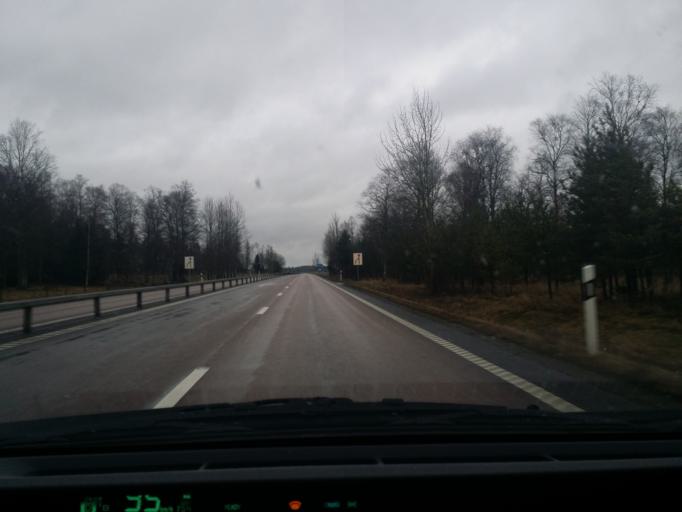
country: SE
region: Vaestmanland
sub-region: Sala Kommun
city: Sala
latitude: 59.8410
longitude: 16.5333
